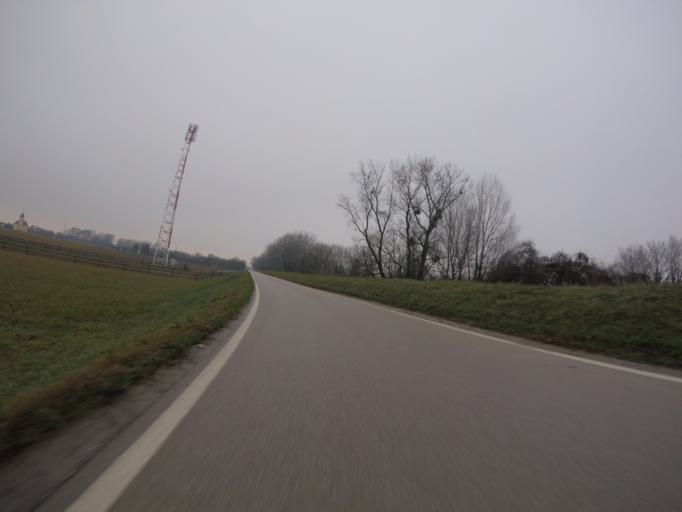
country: HR
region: Zagrebacka
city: Kuce
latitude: 45.6885
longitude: 16.2436
